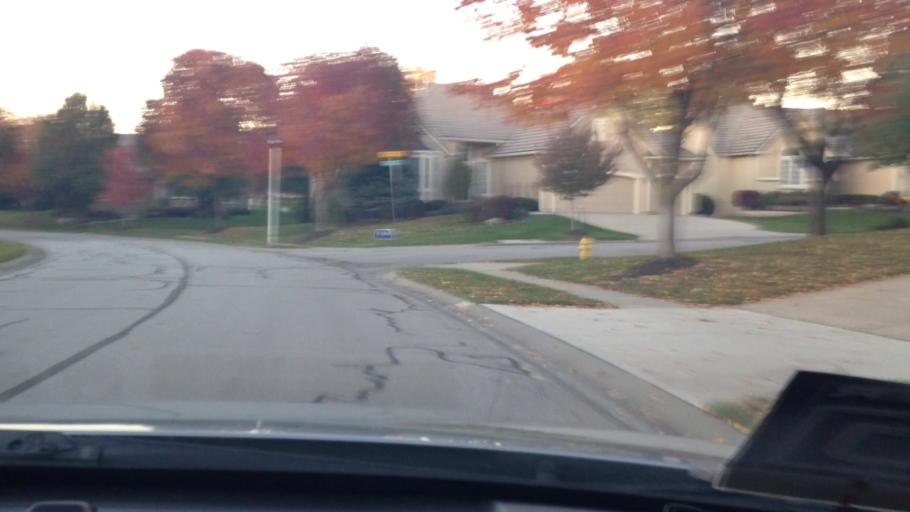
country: US
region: Kansas
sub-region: Johnson County
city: Lenexa
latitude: 38.8675
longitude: -94.7205
